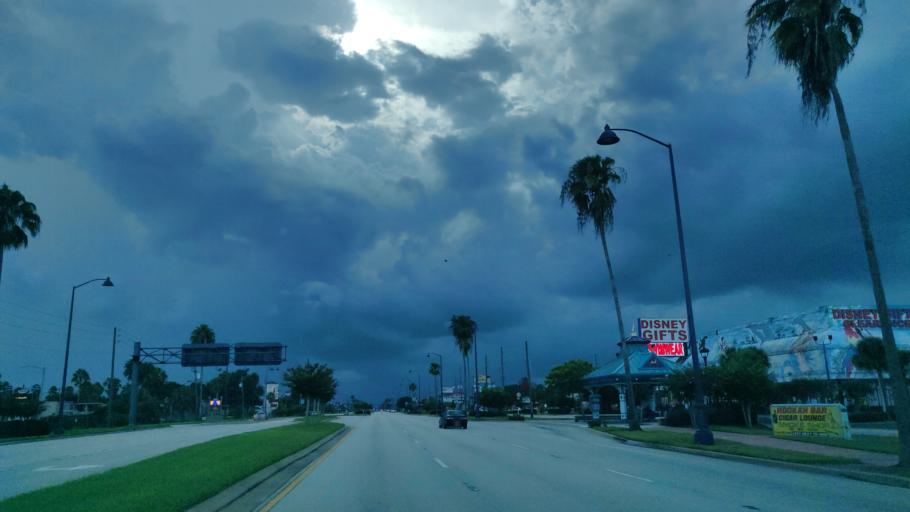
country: US
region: Florida
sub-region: Osceola County
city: Celebration
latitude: 28.3330
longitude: -81.4819
